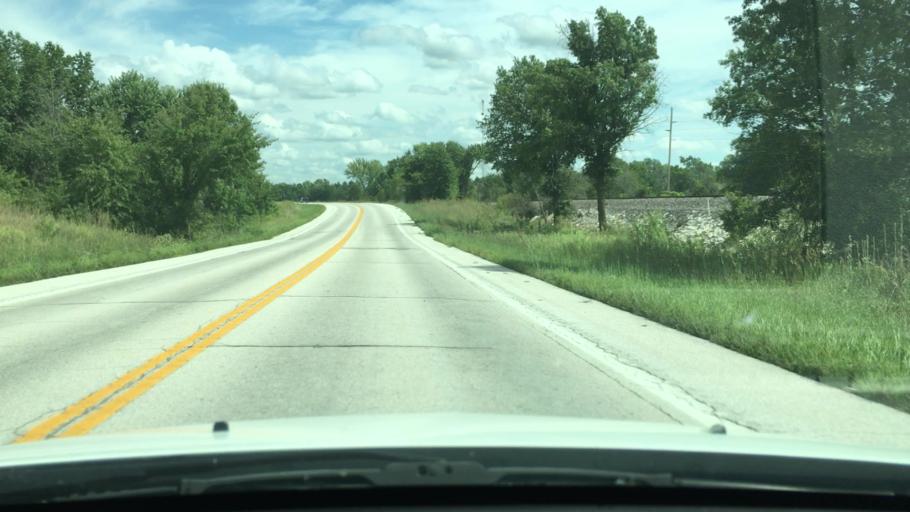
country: US
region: Missouri
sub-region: Audrain County
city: Vandalia
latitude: 39.3366
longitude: -91.4240
